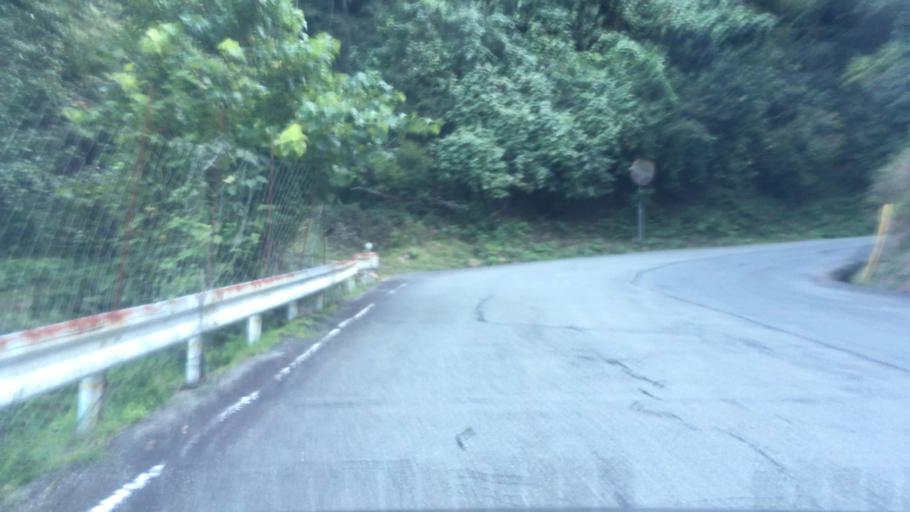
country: JP
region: Hyogo
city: Toyooka
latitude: 35.6104
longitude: 134.8377
